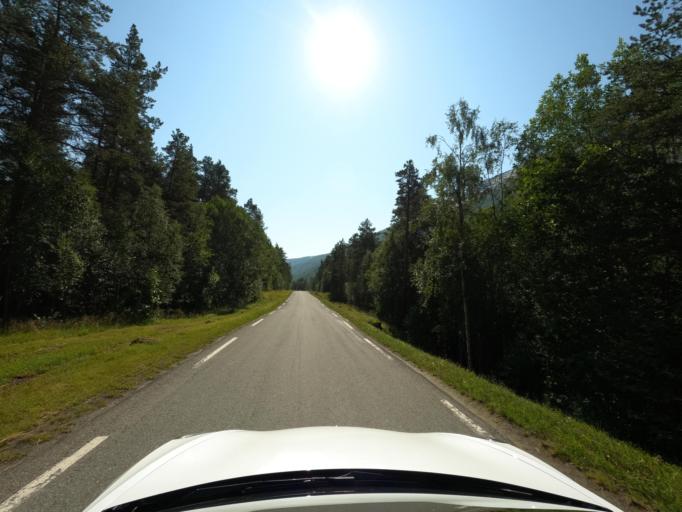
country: NO
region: Nordland
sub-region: Narvik
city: Narvik
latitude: 68.1920
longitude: 17.5541
